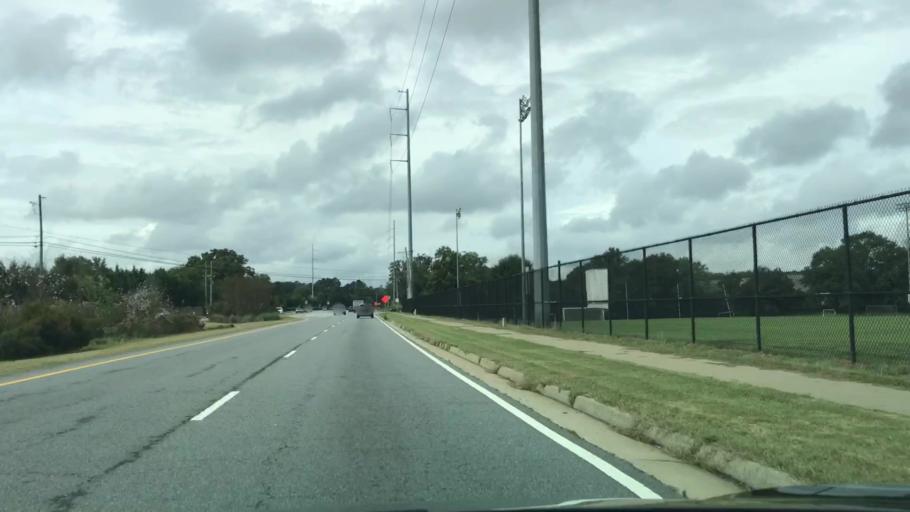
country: US
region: Georgia
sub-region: Gwinnett County
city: Suwanee
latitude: 34.0515
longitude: -84.1183
